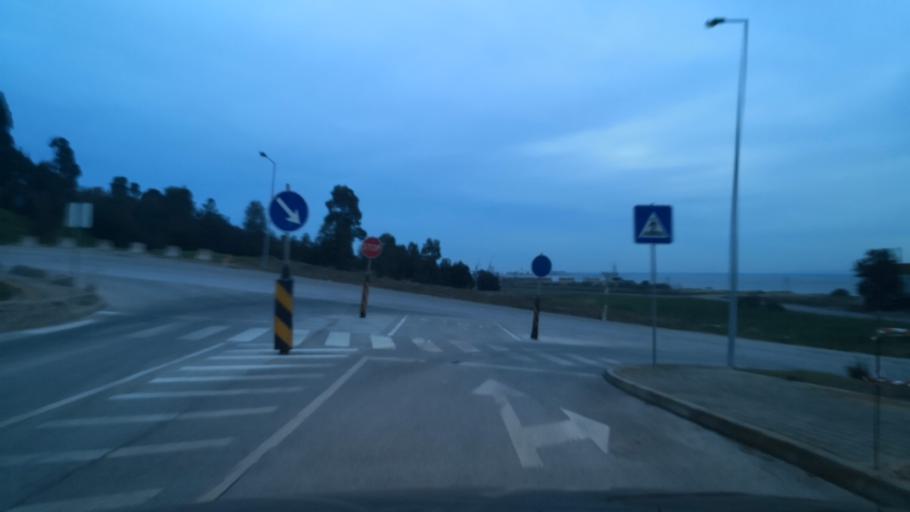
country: PT
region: Setubal
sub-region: Setubal
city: Setubal
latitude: 38.4957
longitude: -8.8331
